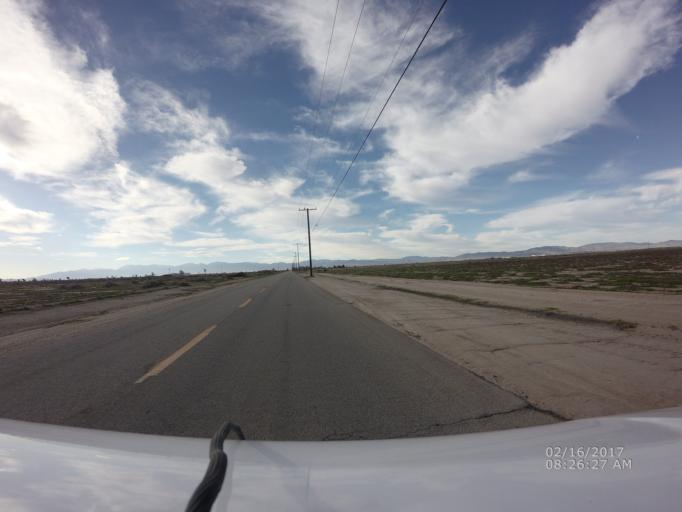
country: US
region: California
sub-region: Los Angeles County
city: Lancaster
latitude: 34.7020
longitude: -118.0055
